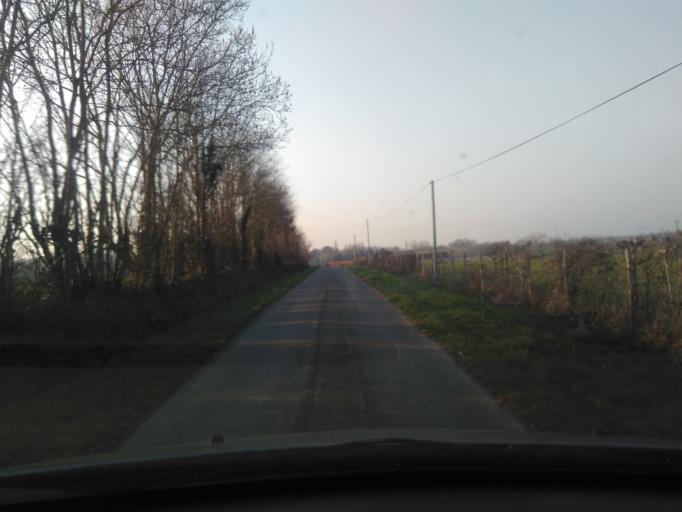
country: FR
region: Pays de la Loire
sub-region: Departement de la Vendee
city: Chantonnay
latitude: 46.6585
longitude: -1.0049
